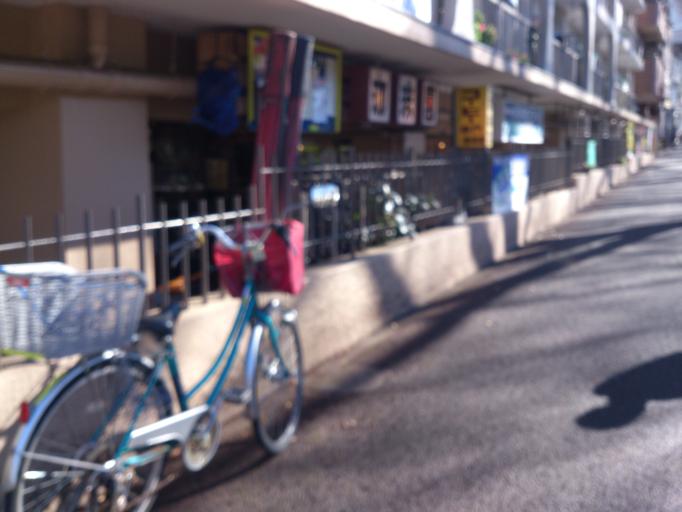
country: JP
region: Chiba
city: Matsudo
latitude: 35.8003
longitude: 139.9517
